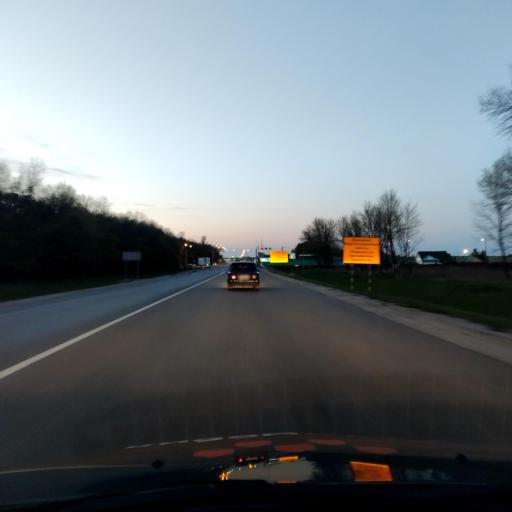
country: RU
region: Orjol
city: Zmiyevka
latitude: 52.7054
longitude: 36.3649
